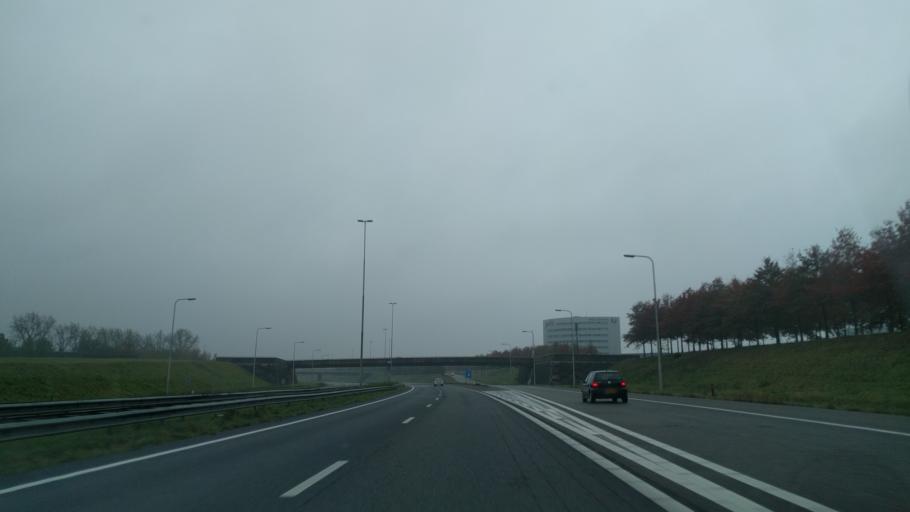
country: NL
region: North Brabant
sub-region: Gemeente Zundert
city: Zundert
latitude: 51.5715
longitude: 4.6676
